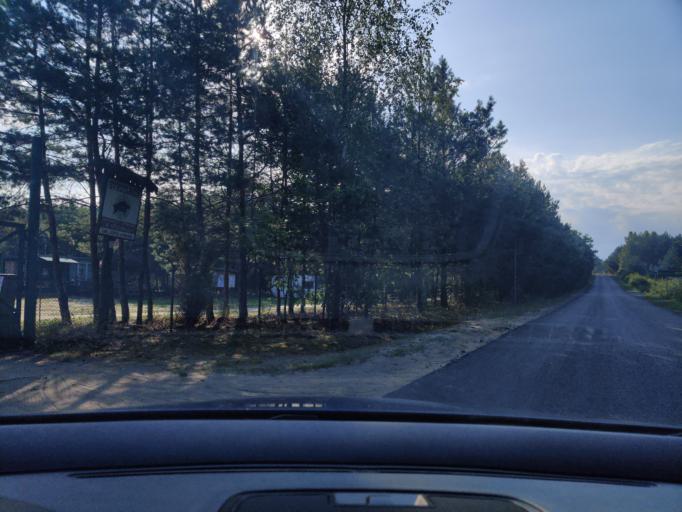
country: PL
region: Greater Poland Voivodeship
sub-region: Powiat koninski
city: Krzymow
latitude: 52.1765
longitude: 18.3374
